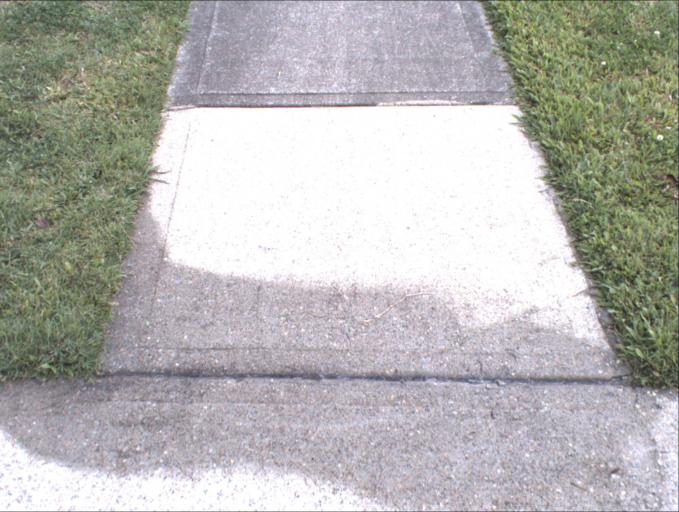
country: AU
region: Queensland
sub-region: Logan
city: Waterford West
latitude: -27.6806
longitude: 153.1519
